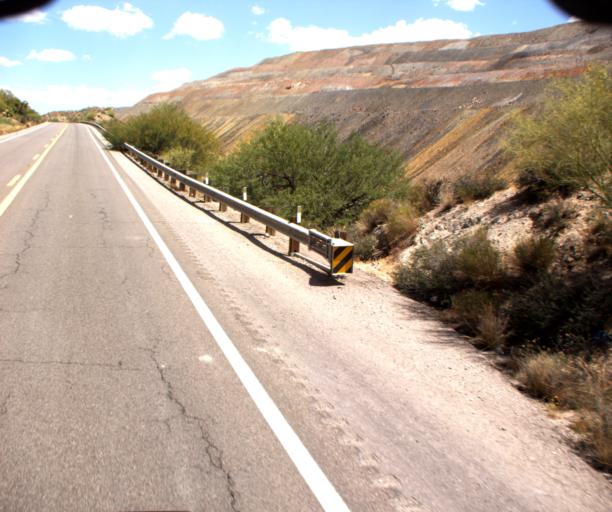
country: US
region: Arizona
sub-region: Pinal County
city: Kearny
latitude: 33.1448
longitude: -110.9918
